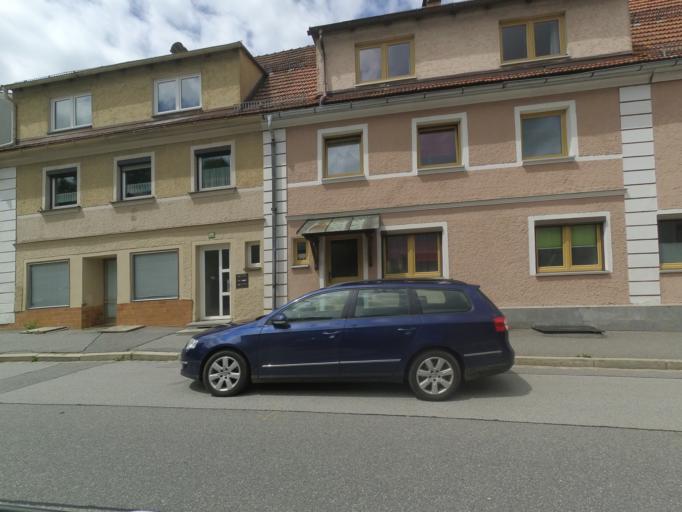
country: DE
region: Bavaria
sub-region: Lower Bavaria
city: Zwiesel
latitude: 49.0187
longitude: 13.2315
